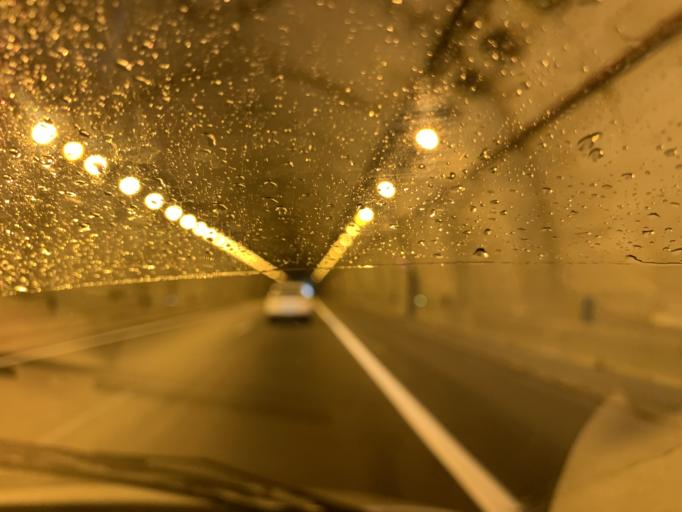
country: ES
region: Asturias
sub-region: Province of Asturias
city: Coana
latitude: 43.5378
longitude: -6.7549
